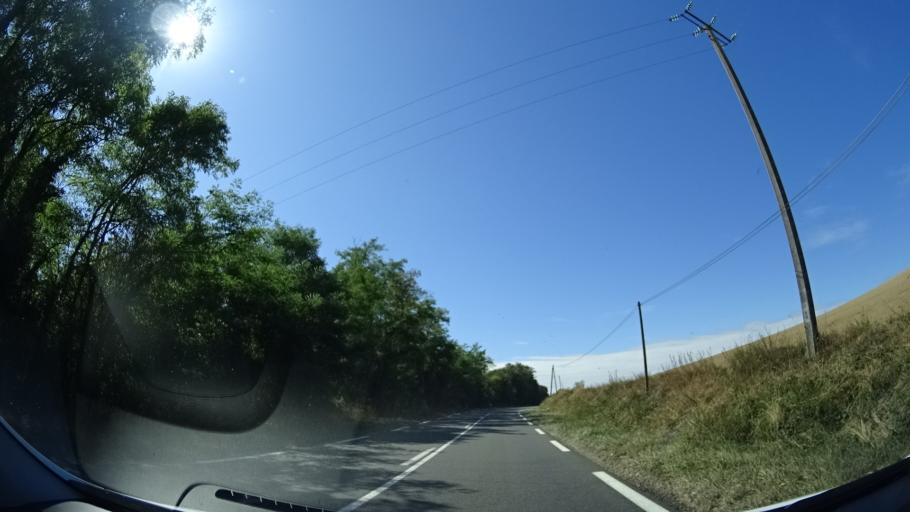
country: FR
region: Centre
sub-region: Departement du Loiret
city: Douchy
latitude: 47.9375
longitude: 3.0720
